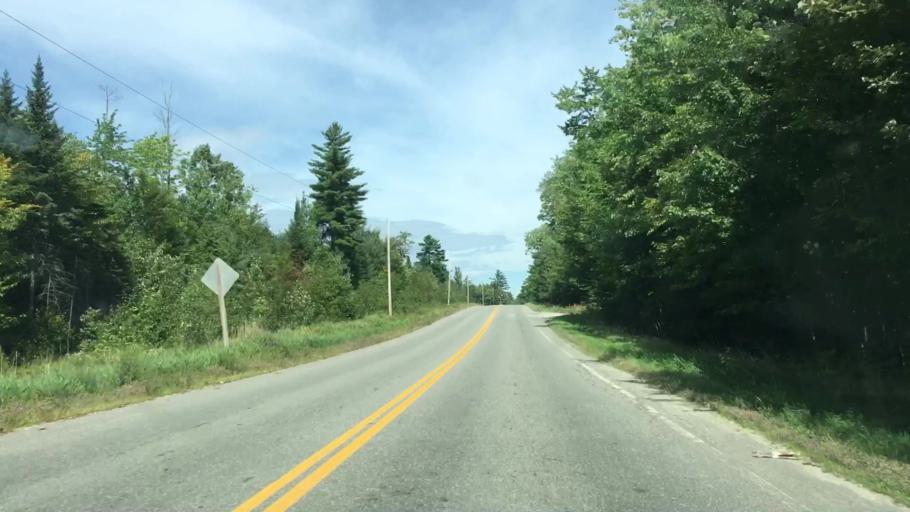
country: US
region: Maine
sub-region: Penobscot County
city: Lincoln
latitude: 45.3717
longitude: -68.5564
